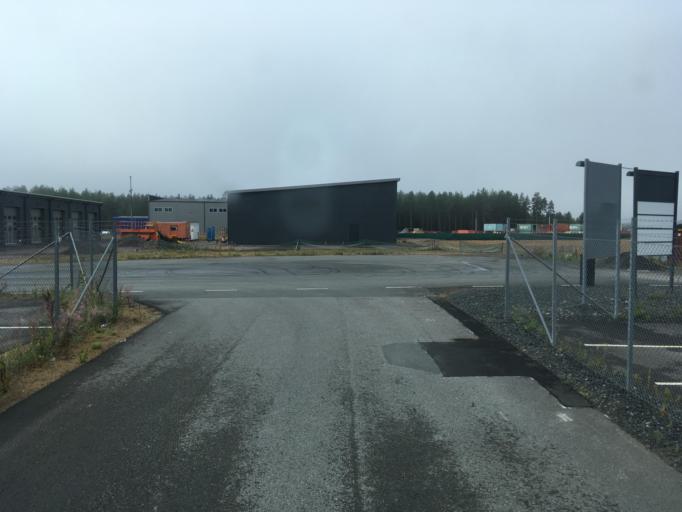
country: SE
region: Joenkoeping
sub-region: Jonkopings Kommun
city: Jonkoping
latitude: 57.7685
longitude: 14.0822
